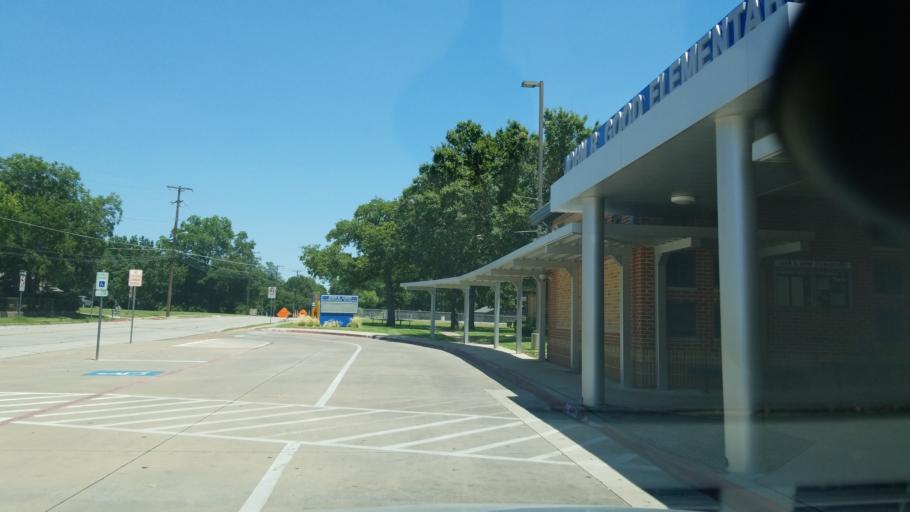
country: US
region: Texas
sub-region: Dallas County
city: Irving
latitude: 32.8229
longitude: -96.9310
